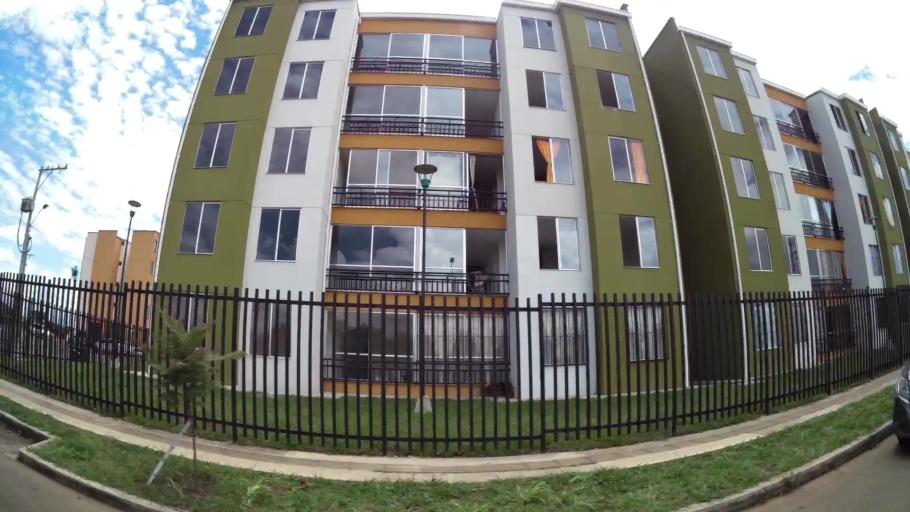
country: CO
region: Valle del Cauca
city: Cali
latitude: 3.3846
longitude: -76.5102
